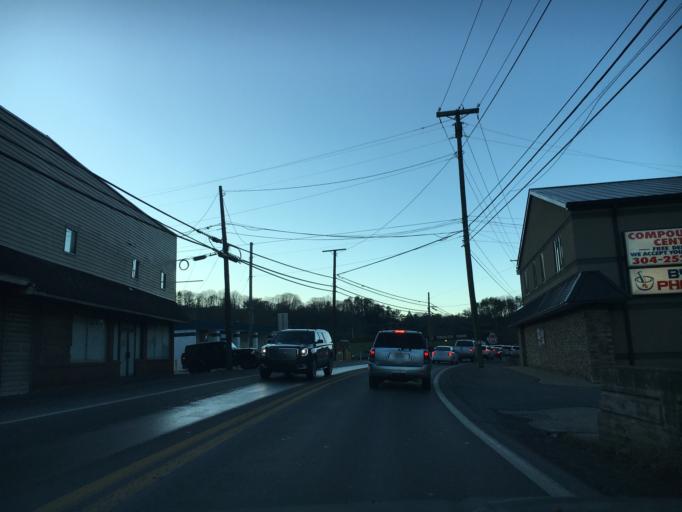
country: US
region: West Virginia
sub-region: Raleigh County
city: Beaver
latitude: 37.7499
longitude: -81.1405
